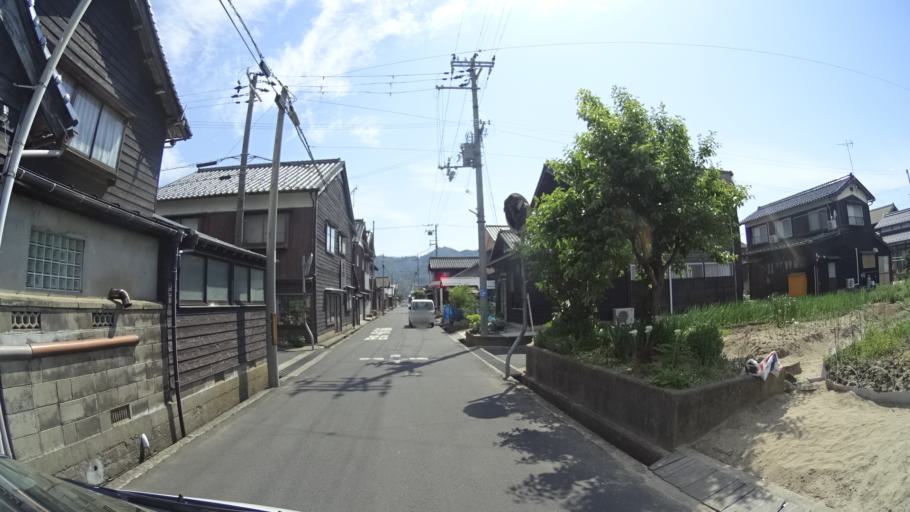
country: JP
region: Kyoto
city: Miyazu
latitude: 35.6866
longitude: 135.0276
